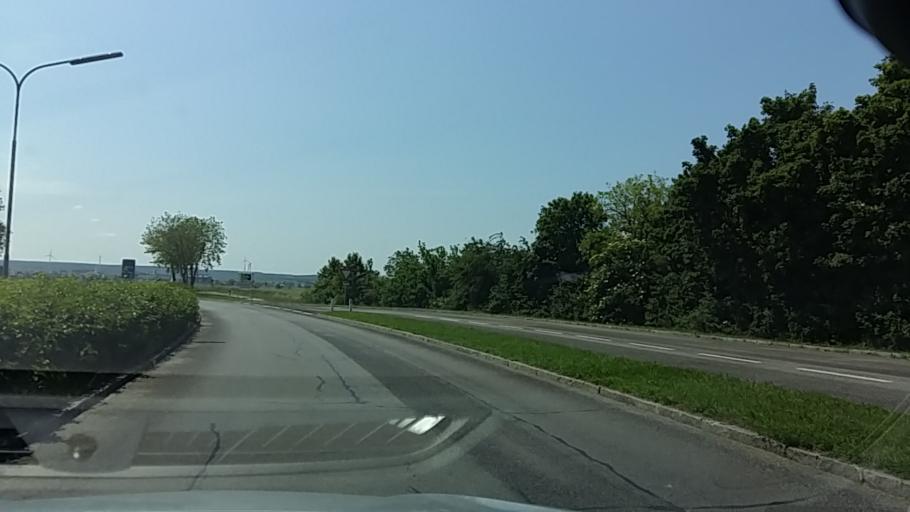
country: AT
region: Burgenland
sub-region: Politischer Bezirk Oberpullendorf
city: Deutschkreutz
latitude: 47.6233
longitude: 16.6232
